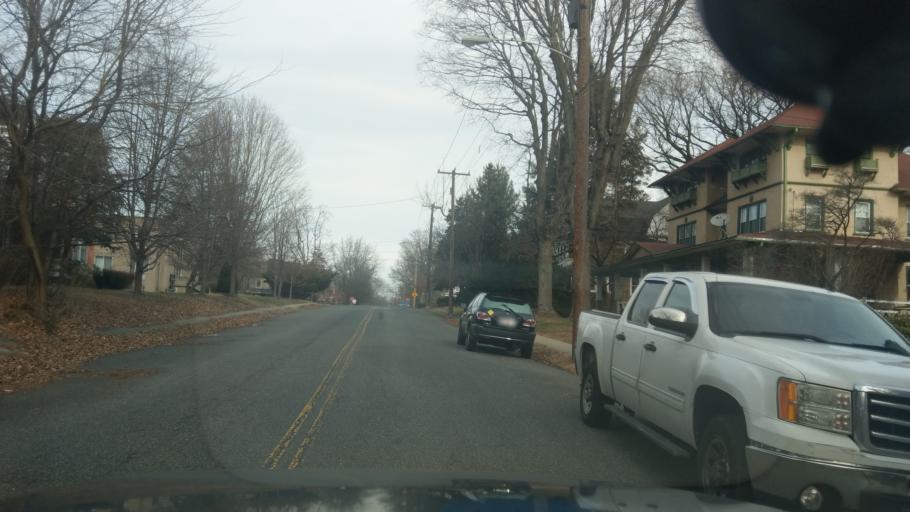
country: US
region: Pennsylvania
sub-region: Montgomery County
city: Wyncote
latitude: 40.0537
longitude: -75.1351
